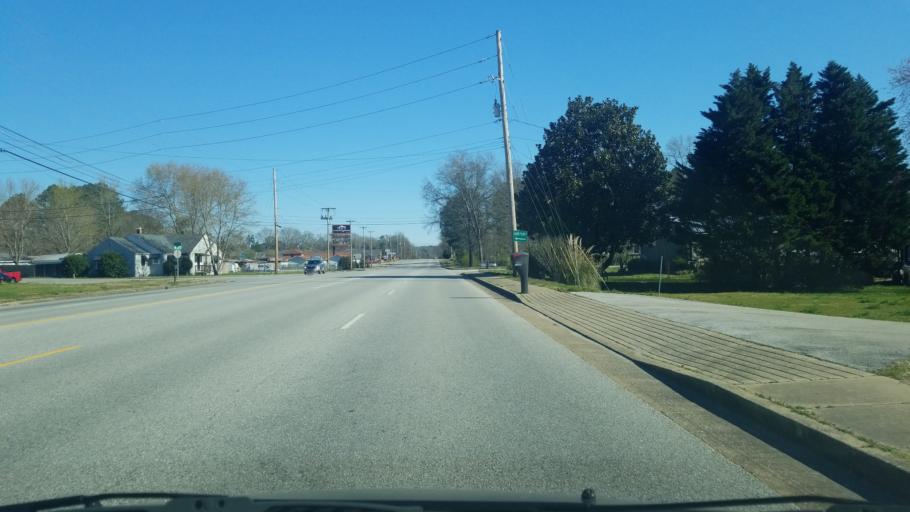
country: US
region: Tennessee
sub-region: Hamilton County
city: Middle Valley
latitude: 35.1855
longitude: -85.1684
